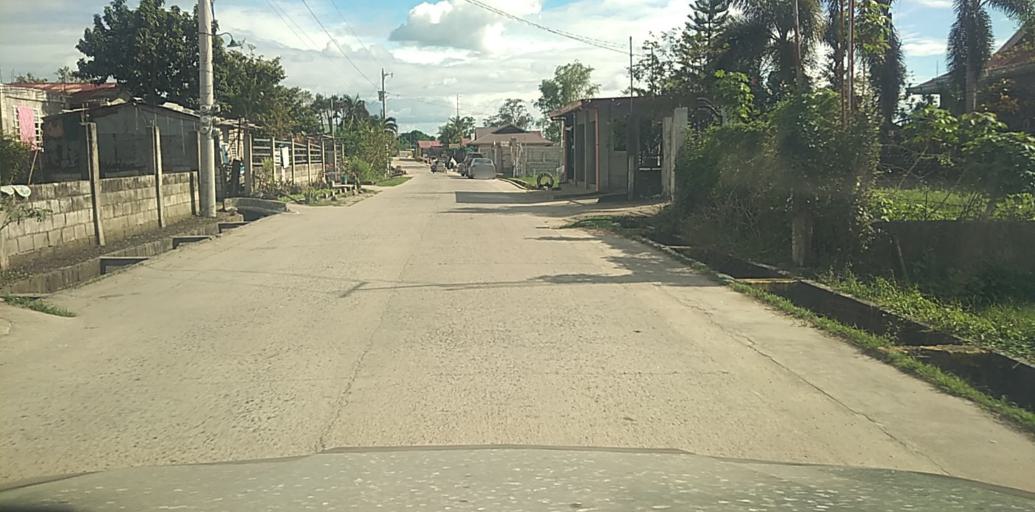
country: PH
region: Central Luzon
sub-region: Province of Pampanga
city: Panlinlang
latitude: 15.1873
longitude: 120.6929
